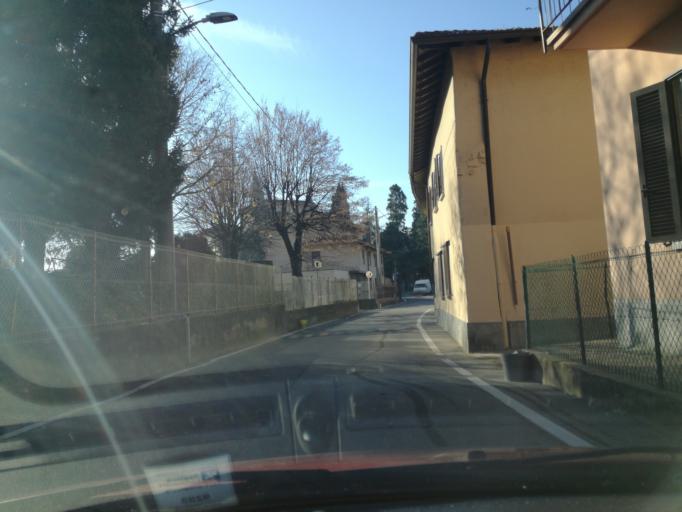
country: IT
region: Lombardy
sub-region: Provincia di Lecco
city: Robbiate
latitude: 45.6967
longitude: 9.4297
